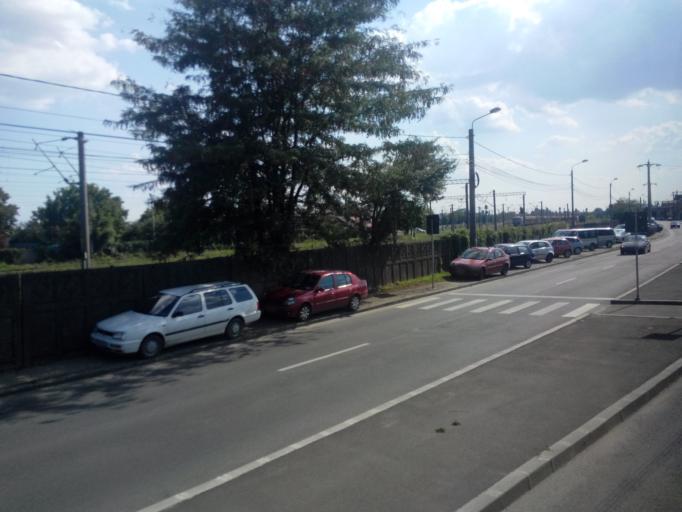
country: RO
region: Timis
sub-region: Comuna Dumbravita
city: Dumbravita
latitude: 45.7723
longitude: 21.2538
